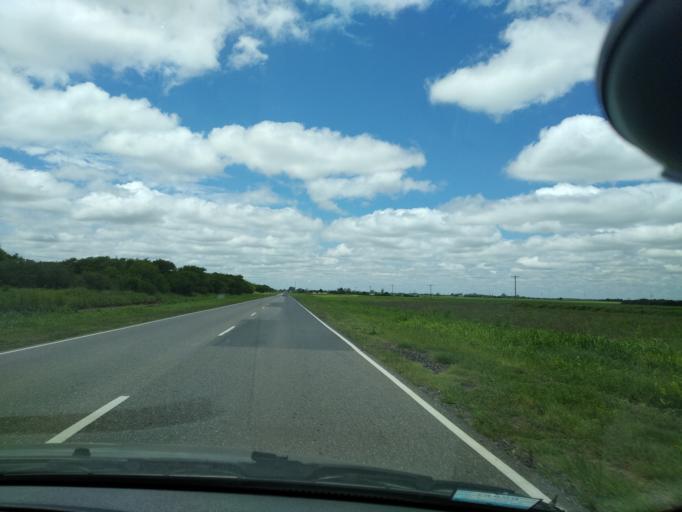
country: AR
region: Cordoba
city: Toledo
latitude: -31.6488
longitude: -64.1161
